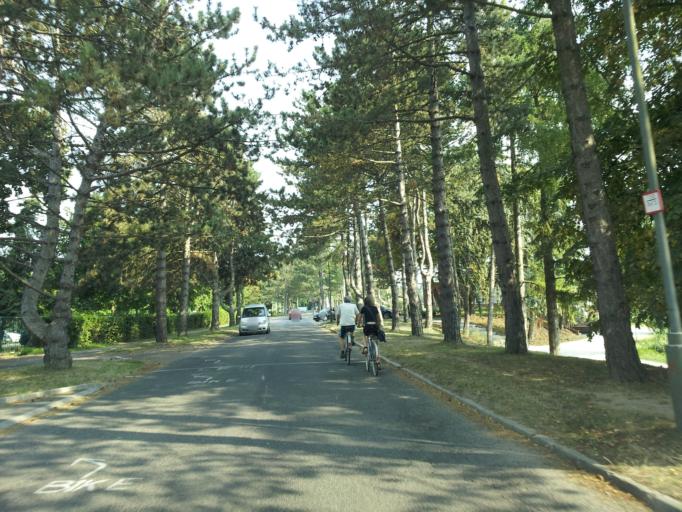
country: HU
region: Vas
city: Szombathely
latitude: 47.2365
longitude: 16.5991
